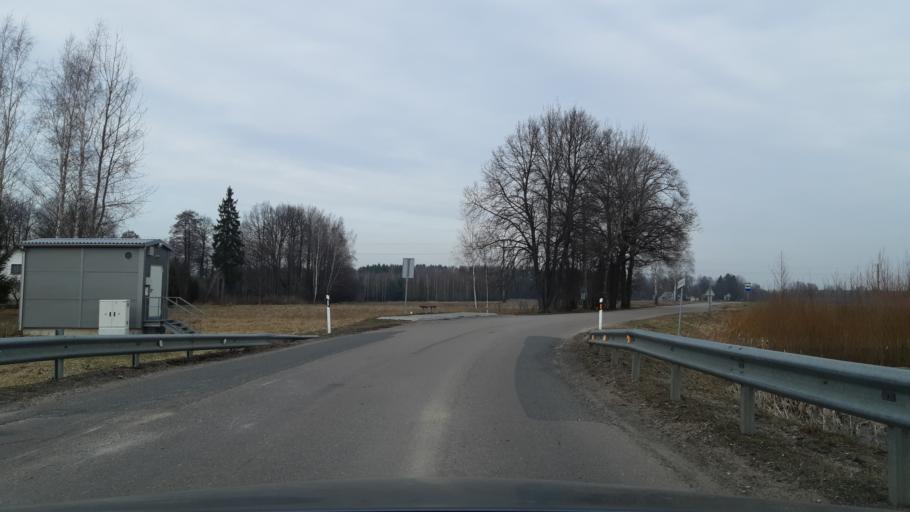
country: LT
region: Marijampoles apskritis
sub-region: Marijampole Municipality
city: Marijampole
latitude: 54.7272
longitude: 23.3362
